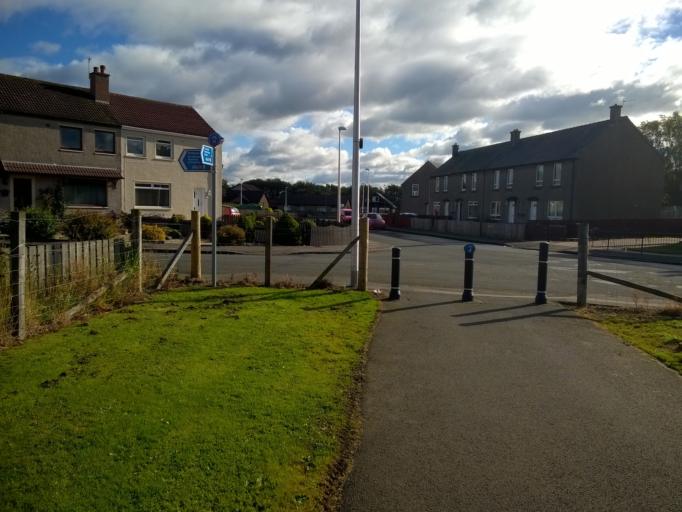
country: GB
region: Scotland
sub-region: West Lothian
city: Bathgate
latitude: 55.8903
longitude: -3.6560
